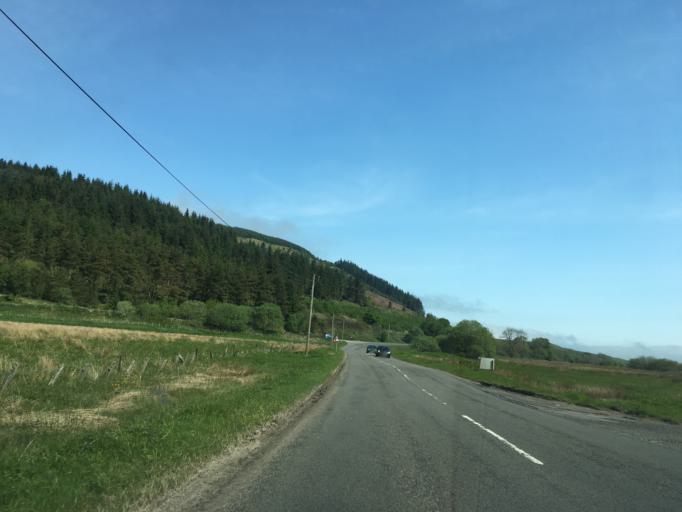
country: GB
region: Scotland
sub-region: South Lanarkshire
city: Biggar
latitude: 55.6559
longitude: -3.4319
